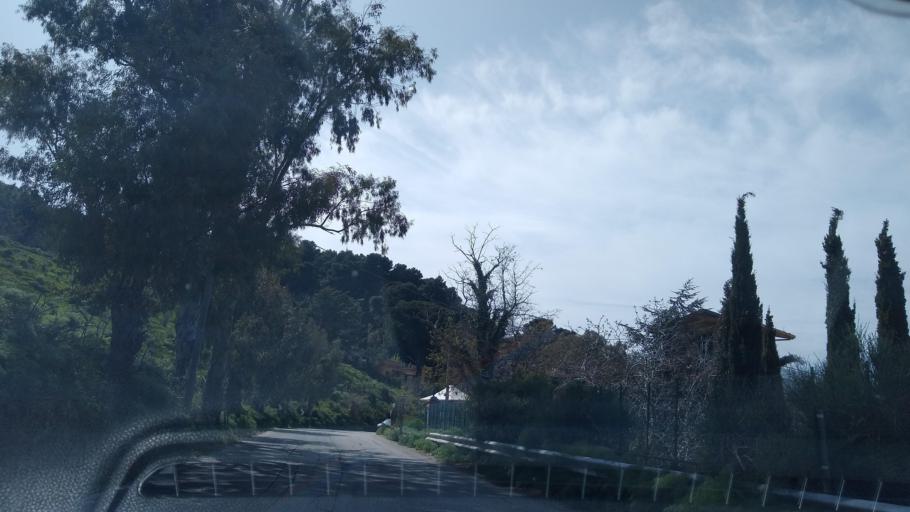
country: IT
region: Sicily
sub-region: Palermo
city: Giacalone
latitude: 38.0322
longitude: 13.2365
